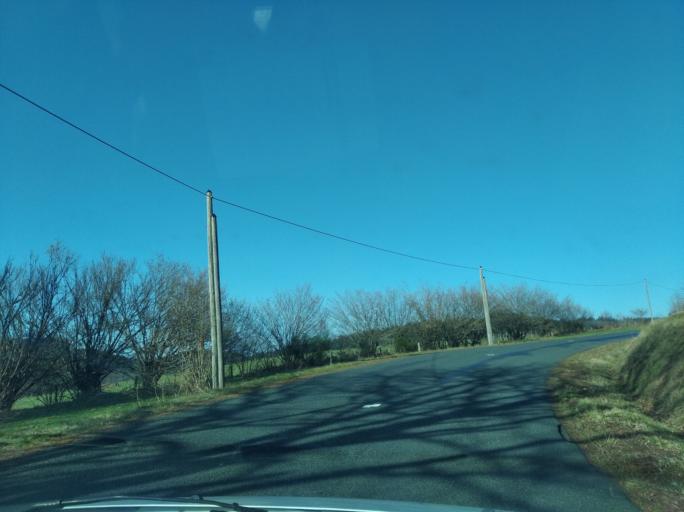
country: FR
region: Auvergne
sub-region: Departement de l'Allier
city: Le Mayet-de-Montagne
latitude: 46.1026
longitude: 3.7756
